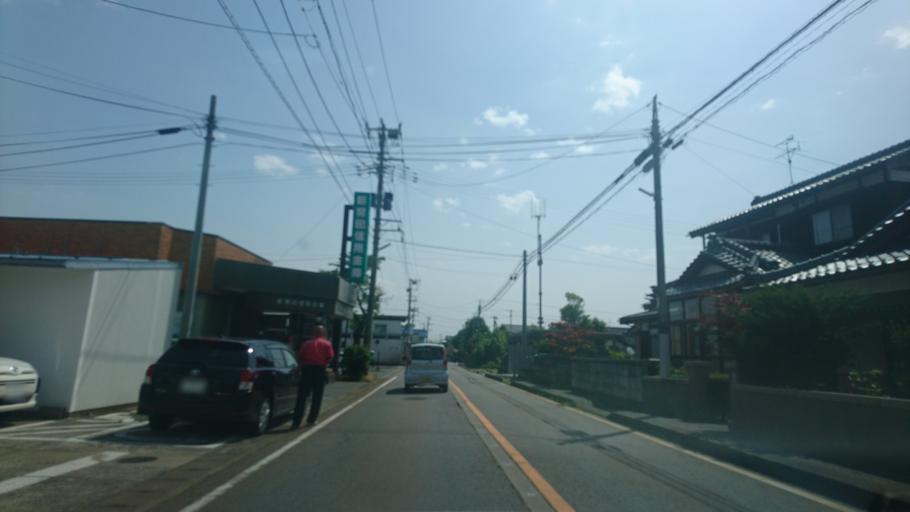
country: JP
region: Niigata
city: Shibata
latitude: 38.0161
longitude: 139.3234
